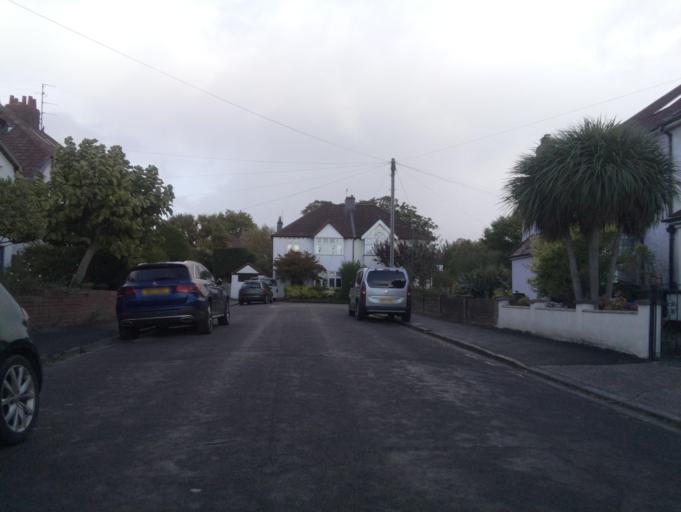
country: GB
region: England
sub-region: Bristol
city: Bristol
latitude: 51.4848
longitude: -2.6073
